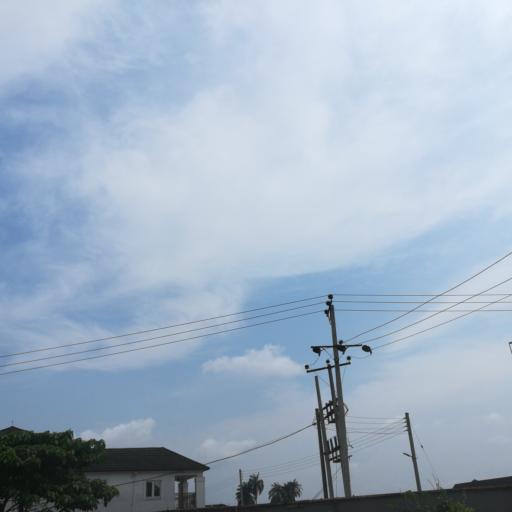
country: NG
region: Rivers
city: Port Harcourt
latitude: 4.8539
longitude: 7.0211
